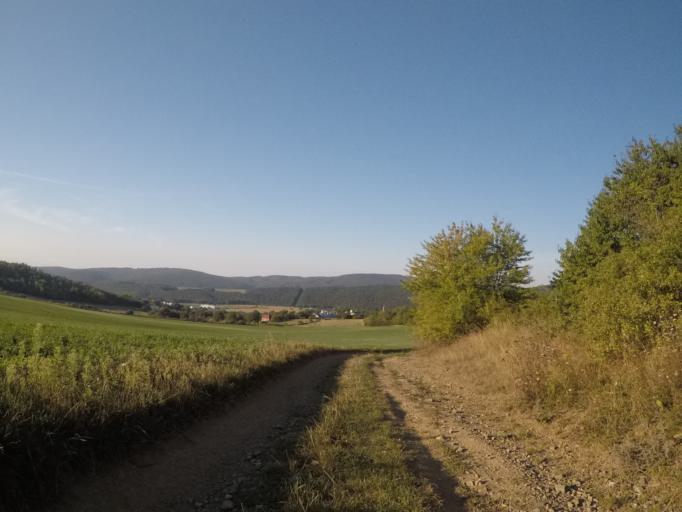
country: SK
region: Kosicky
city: Kosice
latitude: 48.7499
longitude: 21.1283
